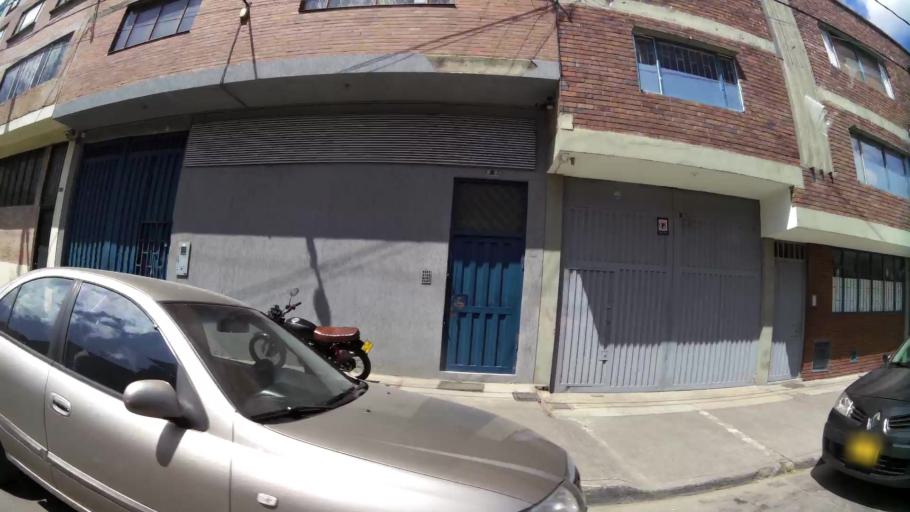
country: CO
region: Bogota D.C.
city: Bogota
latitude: 4.6344
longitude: -74.1091
